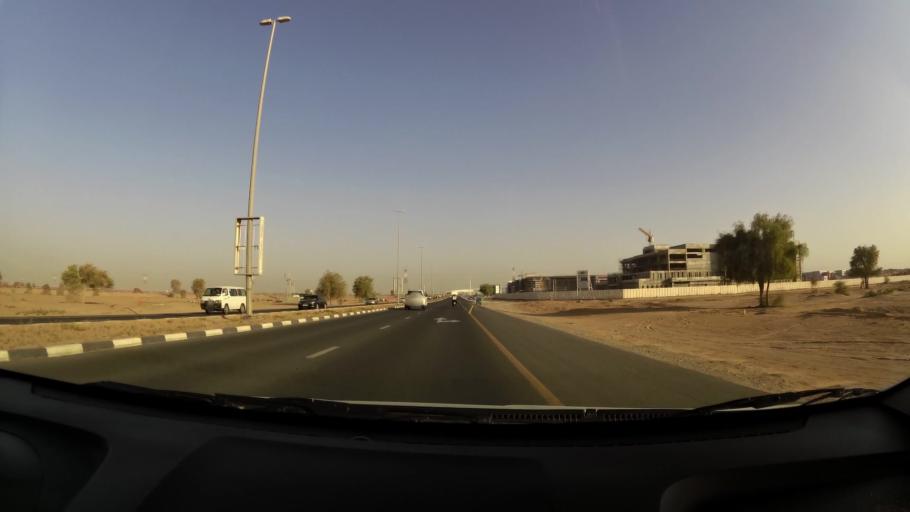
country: AE
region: Ajman
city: Ajman
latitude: 25.3699
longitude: 55.5104
